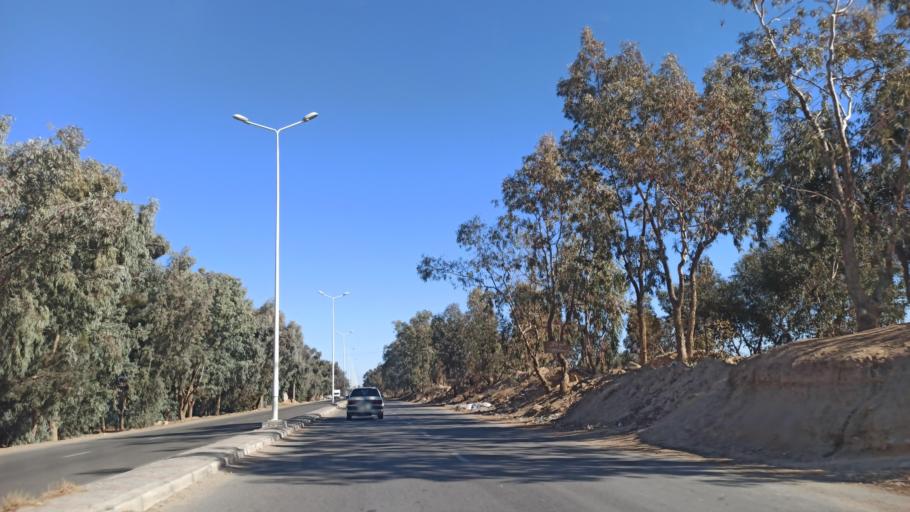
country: TN
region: Gafsa
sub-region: Gafsa Municipality
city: Gafsa
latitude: 34.4040
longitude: 8.7288
